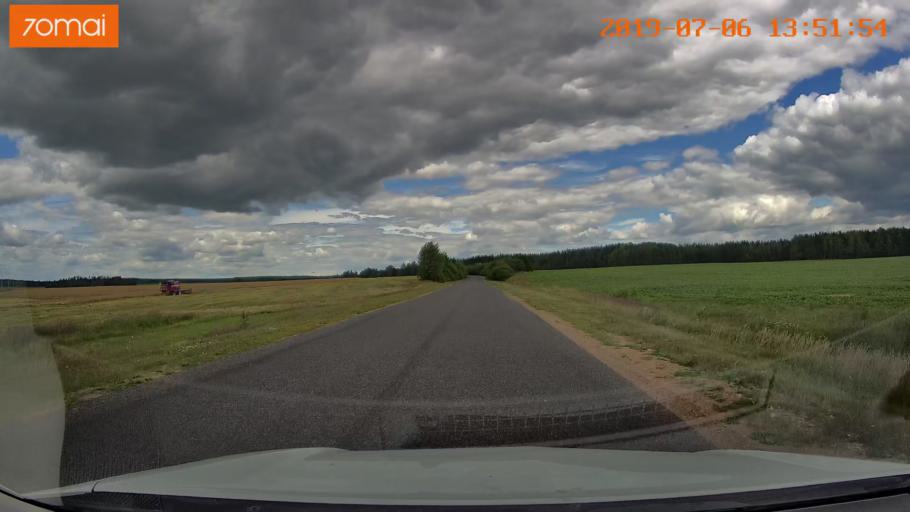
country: BY
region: Minsk
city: Ivyanyets
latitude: 53.7138
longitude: 26.8293
